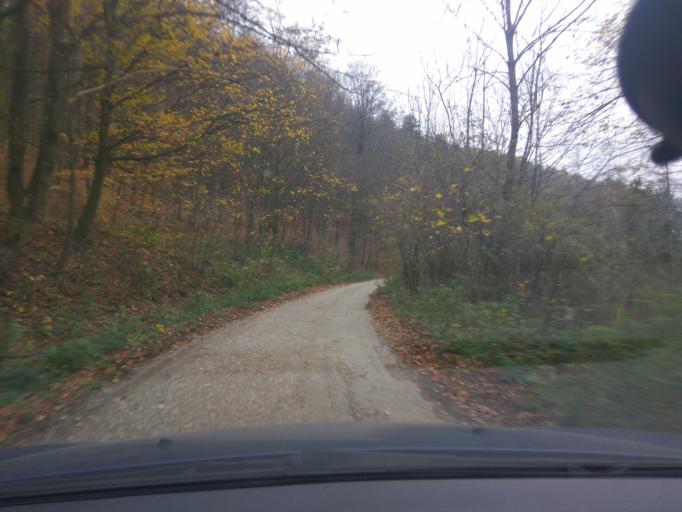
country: SK
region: Trnavsky
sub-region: Okres Trnava
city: Piestany
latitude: 48.6027
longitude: 17.9331
